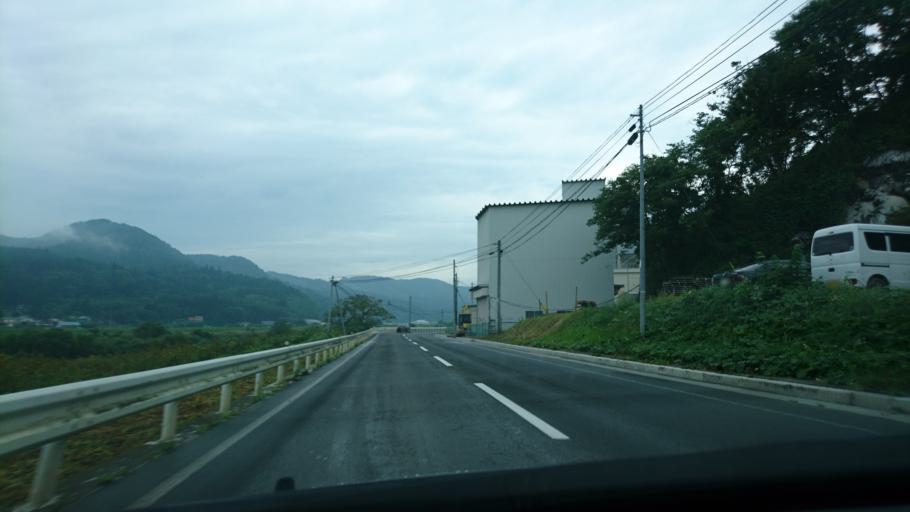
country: JP
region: Iwate
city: Ichinoseki
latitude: 38.9641
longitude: 141.2451
